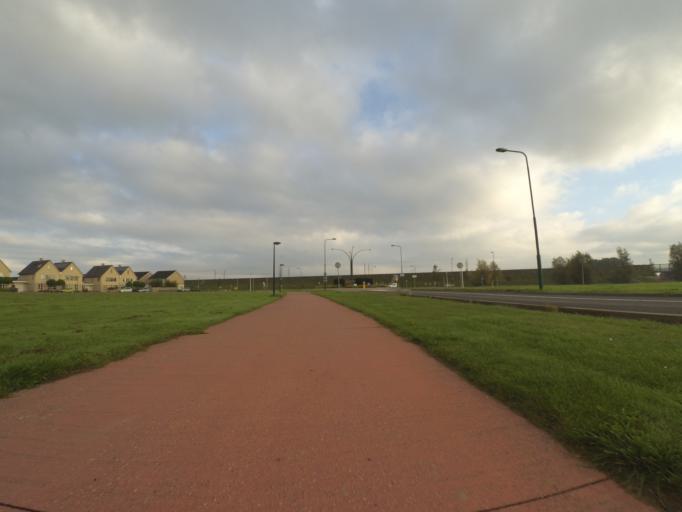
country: NL
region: Flevoland
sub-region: Gemeente Dronten
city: Dronten
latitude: 52.5379
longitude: 5.6936
